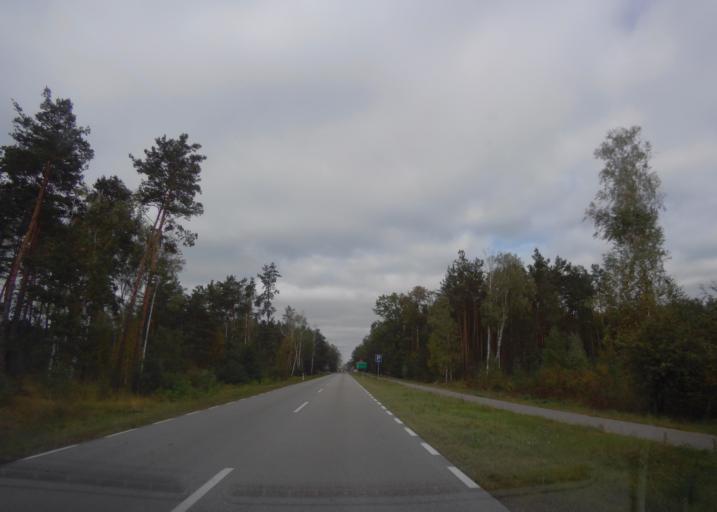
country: PL
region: Lublin Voivodeship
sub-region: Powiat wlodawski
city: Wlodawa
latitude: 51.4883
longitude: 23.5173
